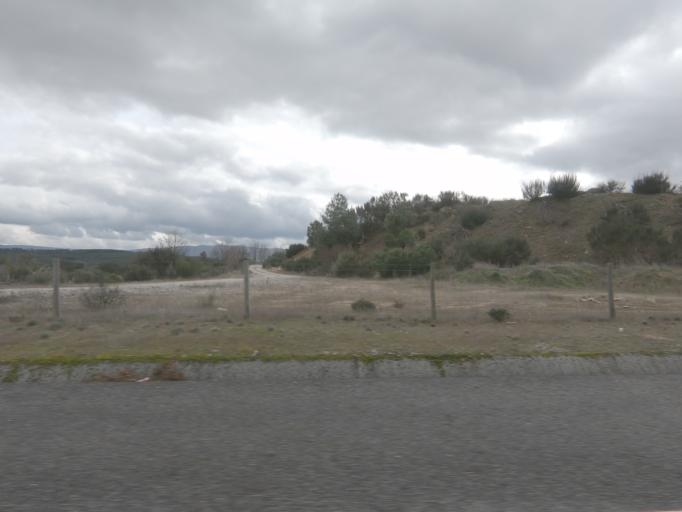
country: PT
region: Vila Real
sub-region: Chaves
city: Chaves
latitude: 41.7331
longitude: -7.5301
